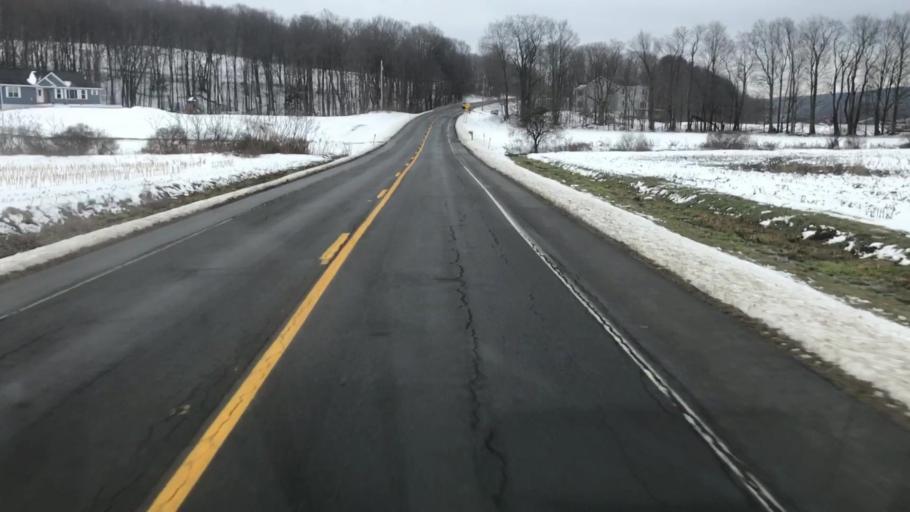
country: US
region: New York
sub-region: Cayuga County
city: Moravia
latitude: 42.6988
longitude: -76.3073
